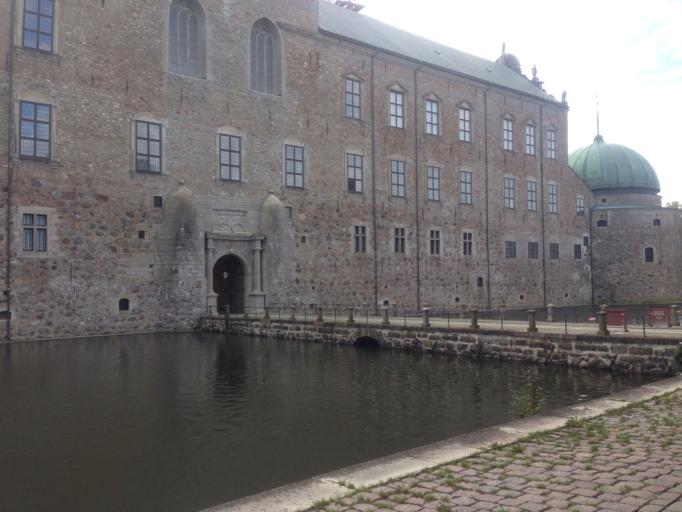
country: SE
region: OEstergoetland
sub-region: Vadstena Kommun
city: Vadstena
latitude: 58.4467
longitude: 14.8833
